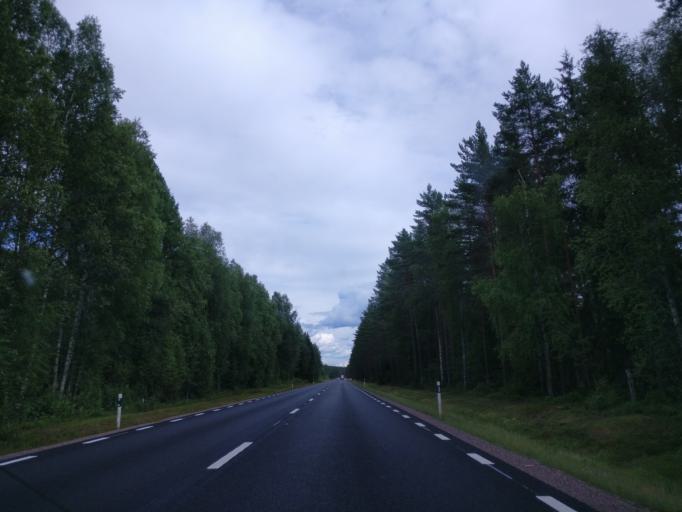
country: SE
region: Vaermland
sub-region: Hagfors Kommun
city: Hagfors
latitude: 60.0515
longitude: 13.5635
